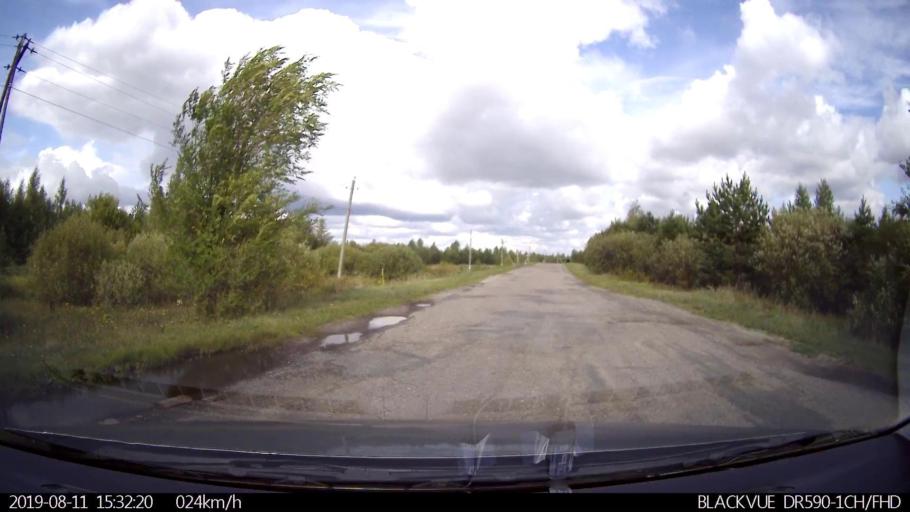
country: RU
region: Ulyanovsk
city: Ignatovka
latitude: 53.8601
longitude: 47.5756
